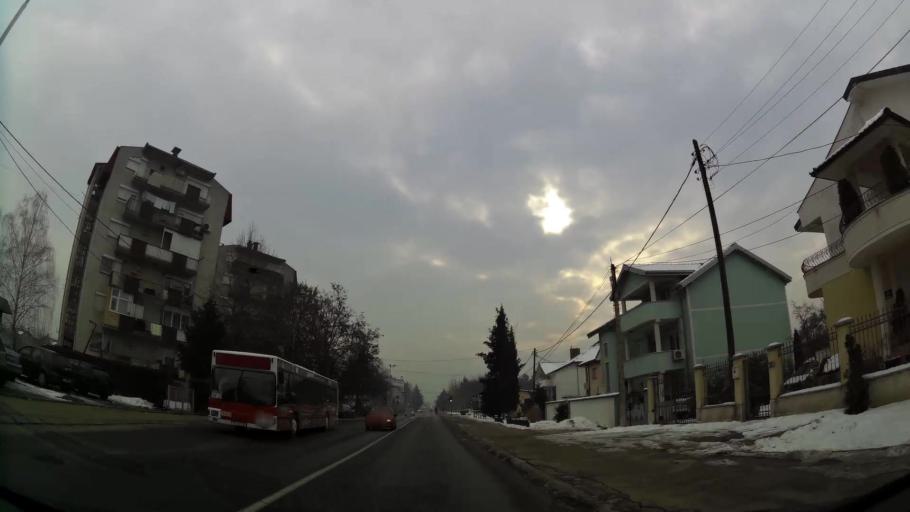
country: MK
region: Saraj
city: Saraj
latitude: 42.0191
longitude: 21.3540
